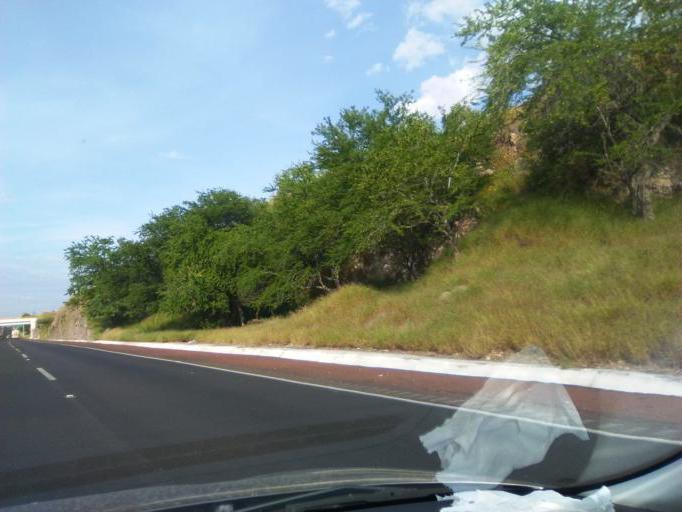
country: MX
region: Morelos
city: Alpuyeca
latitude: 18.7335
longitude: -99.2529
